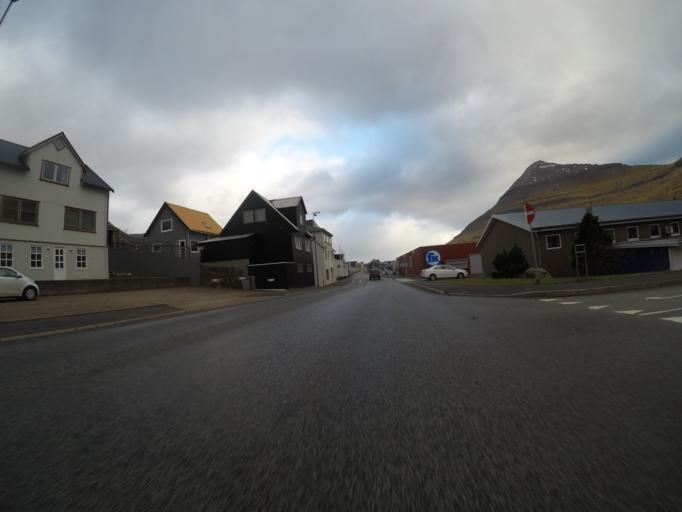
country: FO
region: Nordoyar
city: Klaksvik
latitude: 62.2305
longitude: -6.5883
